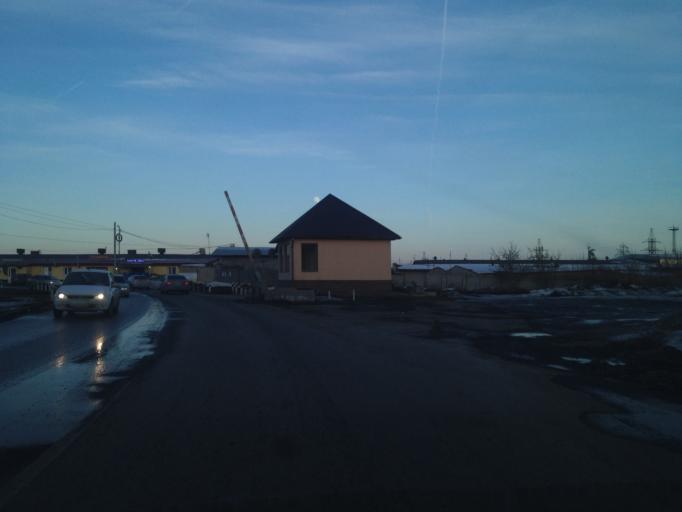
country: RU
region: Sverdlovsk
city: Istok
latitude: 56.7587
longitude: 60.7314
